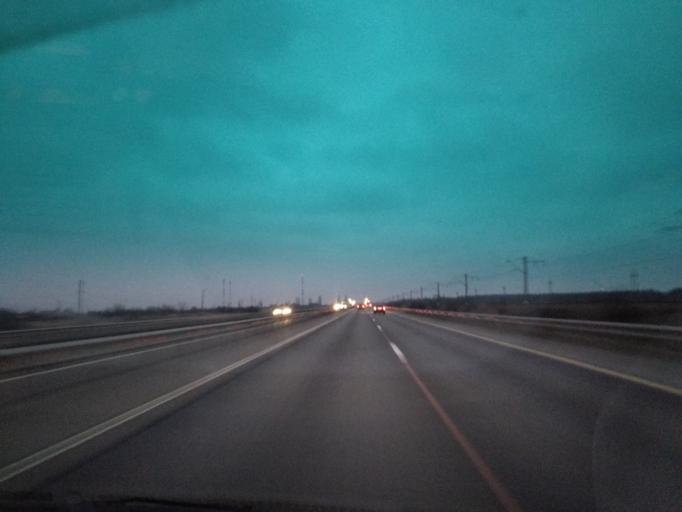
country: RU
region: Adygeya
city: Adygeysk
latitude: 44.8129
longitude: 39.2278
